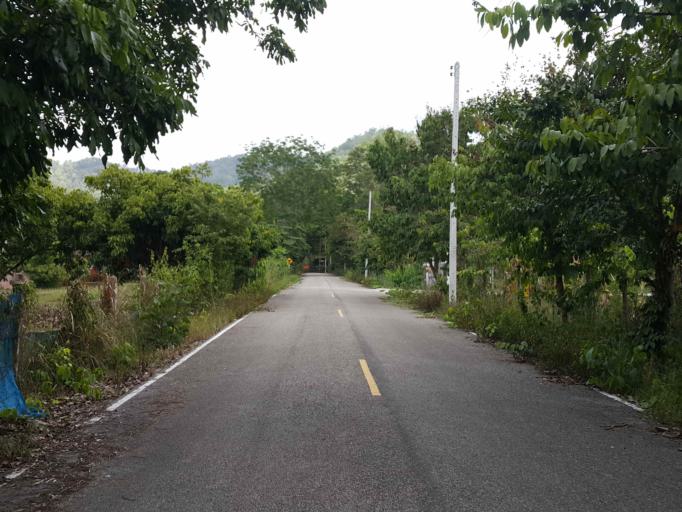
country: TH
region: Chiang Mai
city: Hang Dong
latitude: 18.7606
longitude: 98.9067
